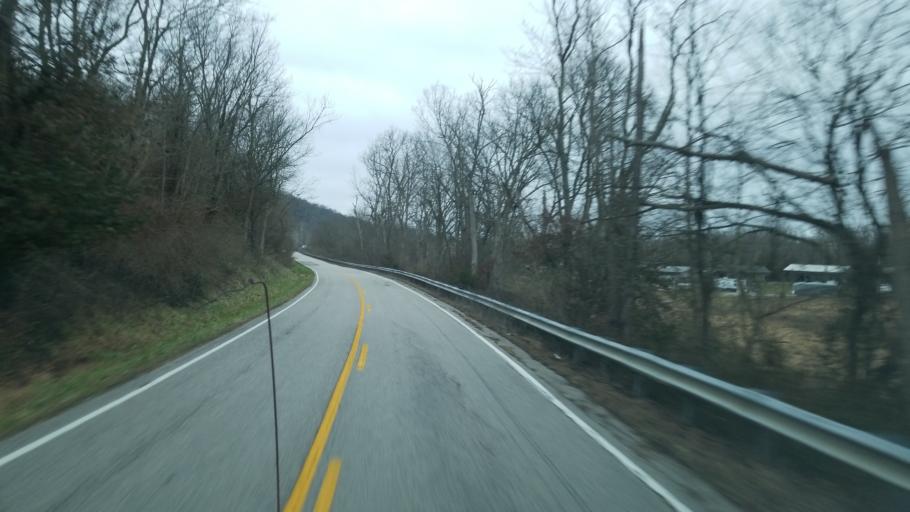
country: US
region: Kentucky
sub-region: Bracken County
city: Brooksville
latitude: 38.7719
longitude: -84.1108
